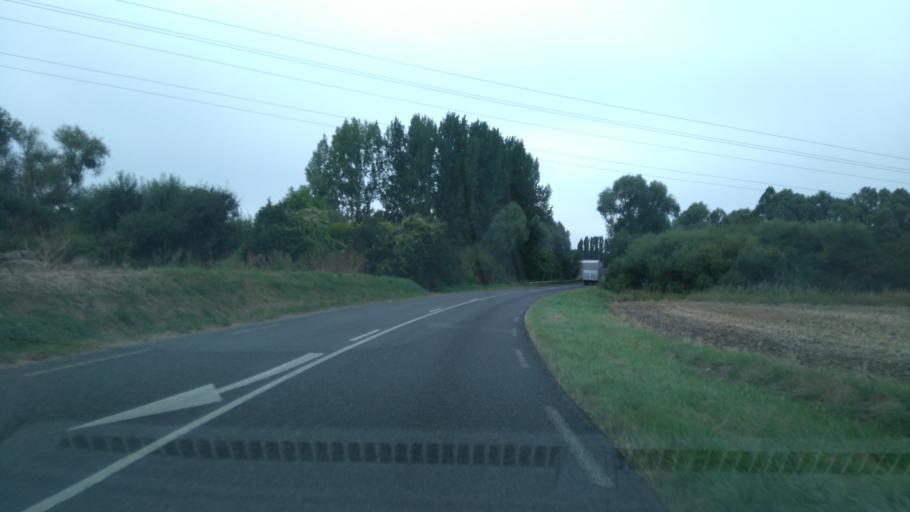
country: FR
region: Picardie
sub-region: Departement de l'Oise
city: Precy-sur-Oise
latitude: 49.1935
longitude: 2.3825
